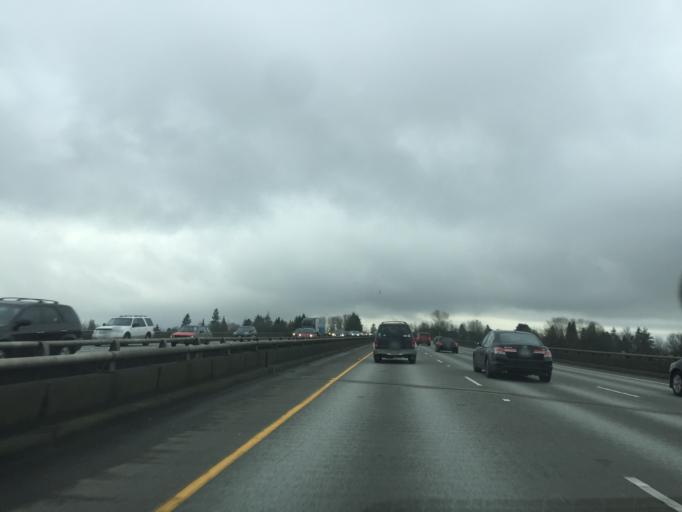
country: US
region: Washington
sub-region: Snohomish County
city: Everett
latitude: 47.9953
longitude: -122.1772
